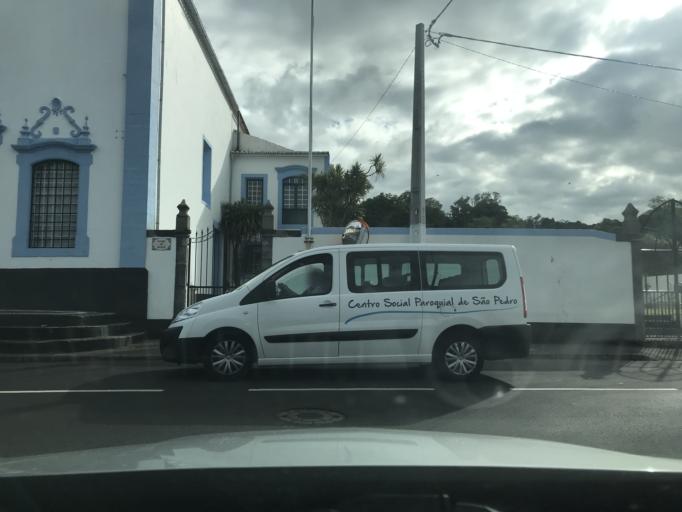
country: PT
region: Azores
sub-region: Angra do Heroismo
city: Angra do Heroismo
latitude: 38.6741
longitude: -27.2489
